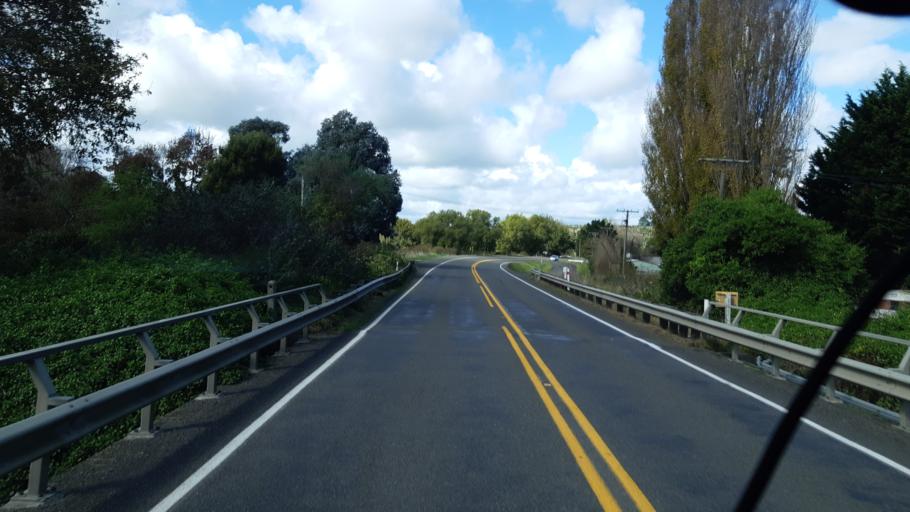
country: NZ
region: Manawatu-Wanganui
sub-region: Wanganui District
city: Wanganui
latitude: -40.0335
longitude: 175.2090
